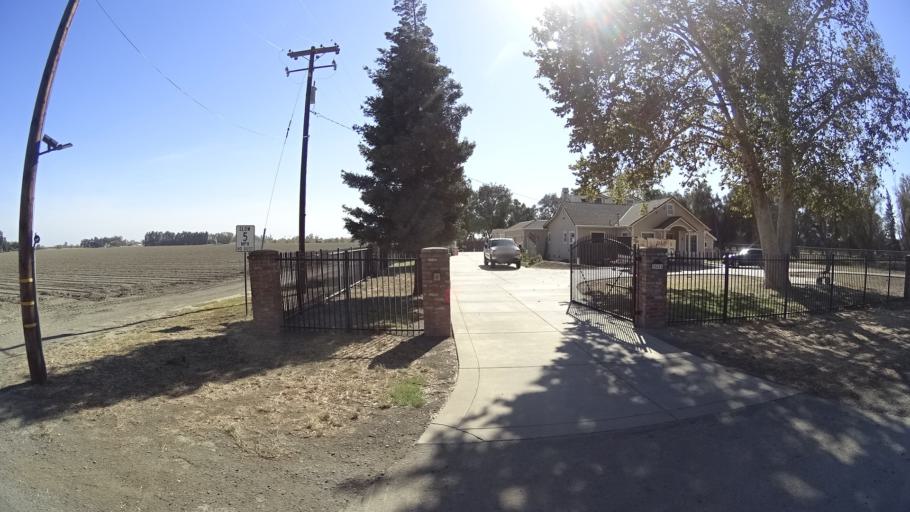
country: US
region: California
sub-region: Yolo County
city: Woodland
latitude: 38.6412
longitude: -121.7918
